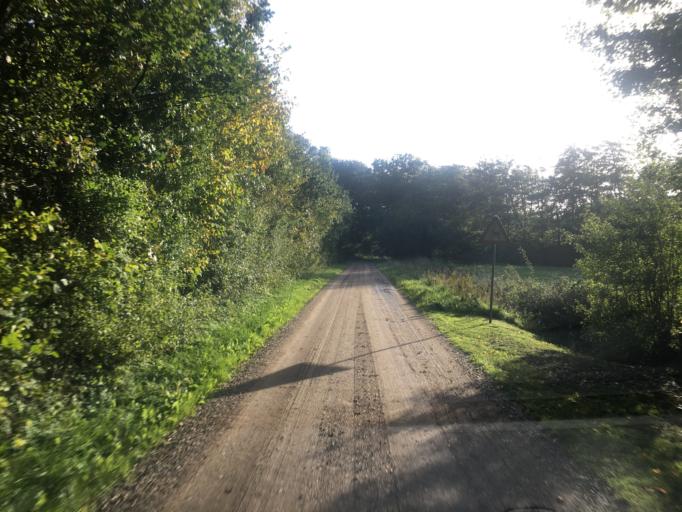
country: DK
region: South Denmark
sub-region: Tonder Kommune
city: Tonder
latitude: 54.9678
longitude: 8.8328
